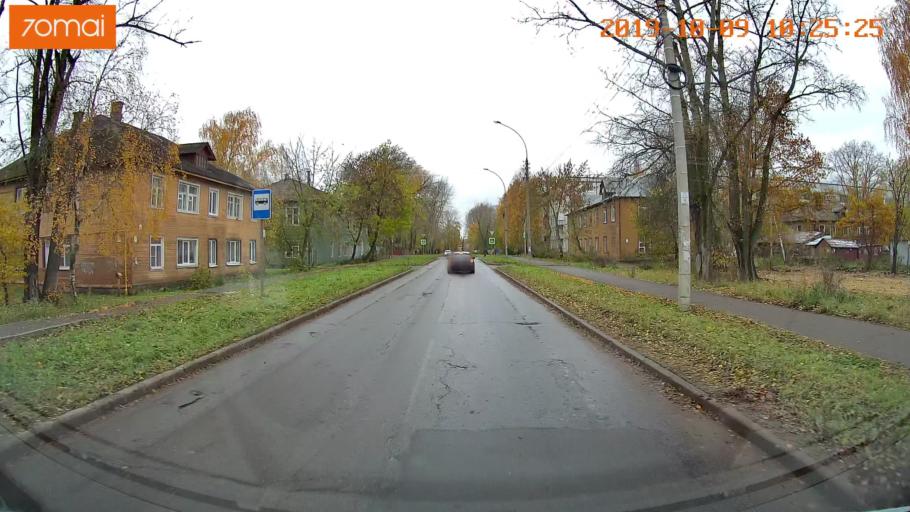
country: RU
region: Vologda
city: Vologda
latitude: 59.2132
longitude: 39.9278
